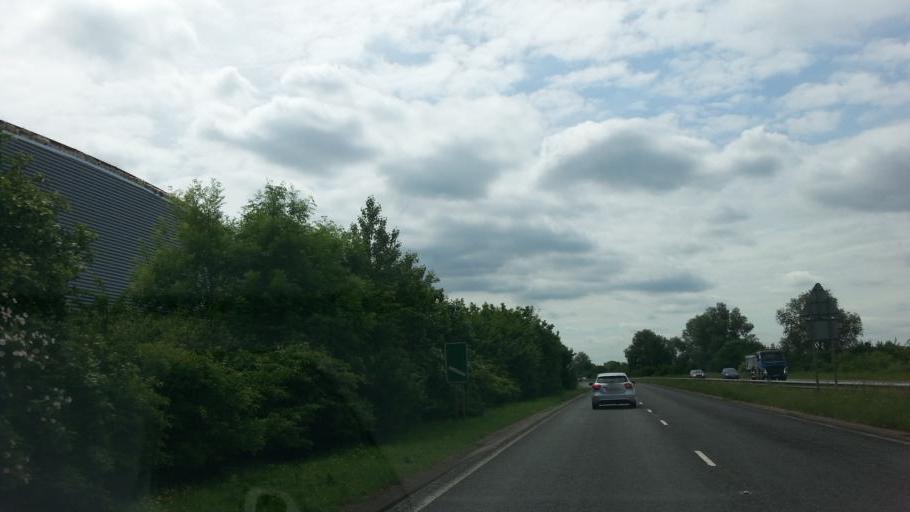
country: GB
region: England
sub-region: Leicestershire
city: Syston
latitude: 52.6946
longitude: -1.0960
